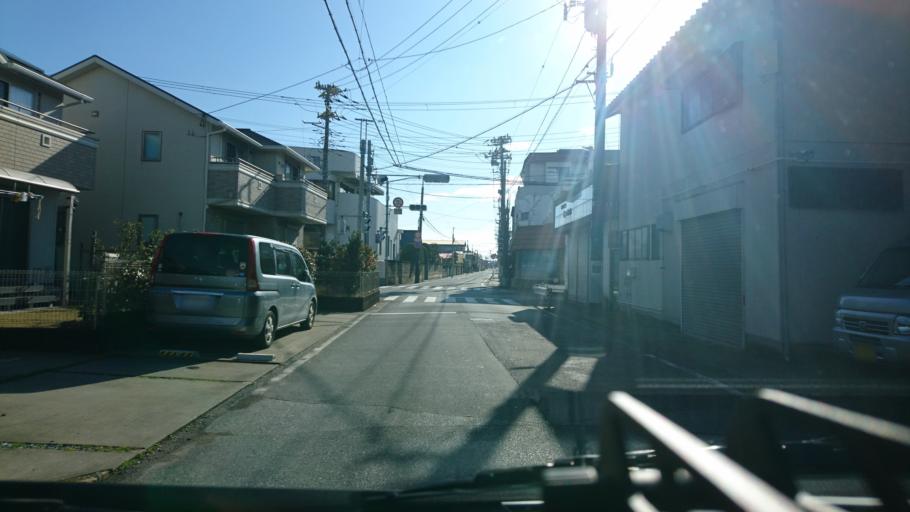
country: JP
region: Chiba
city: Kisarazu
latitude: 35.3776
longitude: 139.9218
